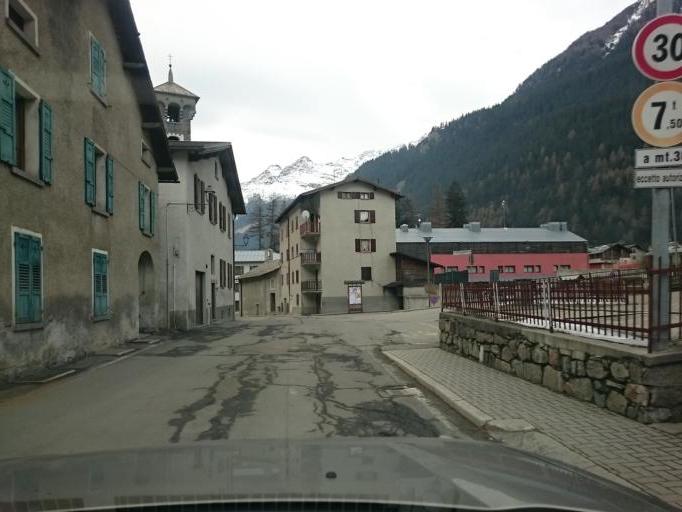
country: IT
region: Lombardy
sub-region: Provincia di Sondrio
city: Valdisotto
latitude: 46.4286
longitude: 10.3561
